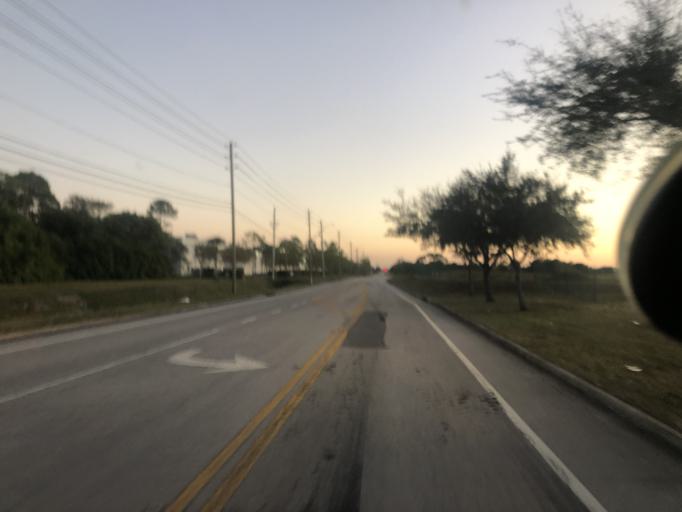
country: US
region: Florida
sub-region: Pinellas County
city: Gandy
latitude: 27.8680
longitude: -82.6553
